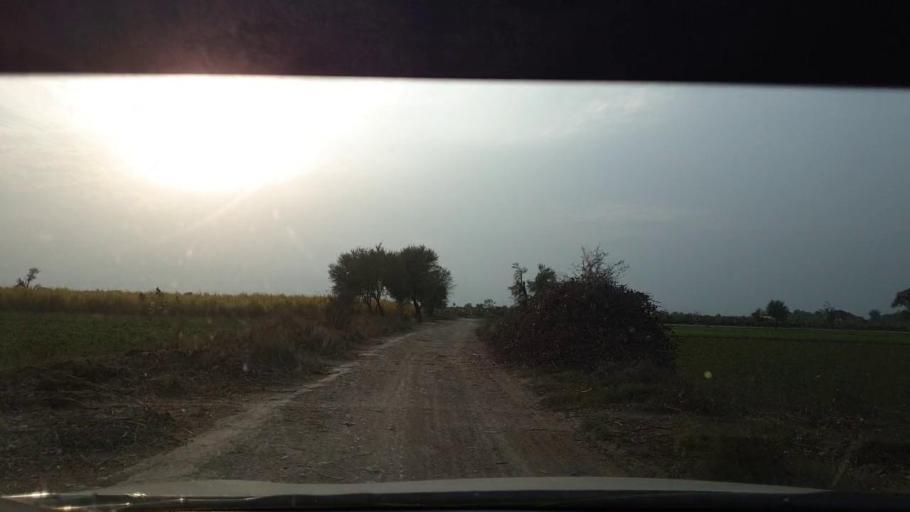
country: PK
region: Sindh
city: Jhol
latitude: 25.9080
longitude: 68.7766
